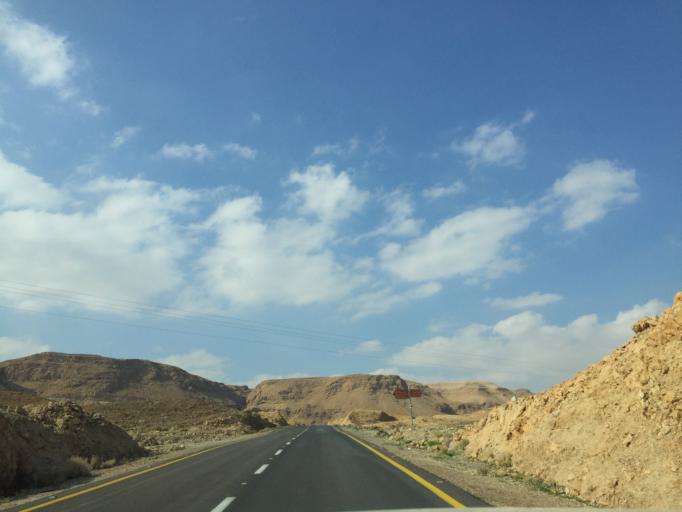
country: IL
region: Southern District
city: `En Boqeq
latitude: 31.3192
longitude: 35.3418
